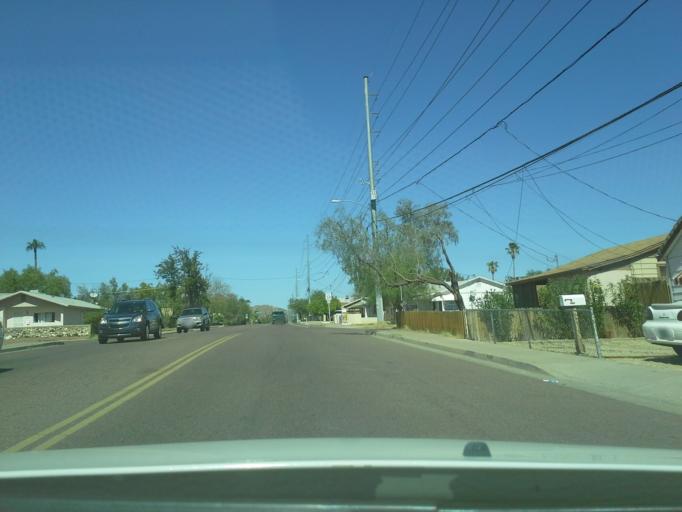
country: US
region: Arizona
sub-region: Maricopa County
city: Paradise Valley
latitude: 33.5683
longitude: -112.0568
